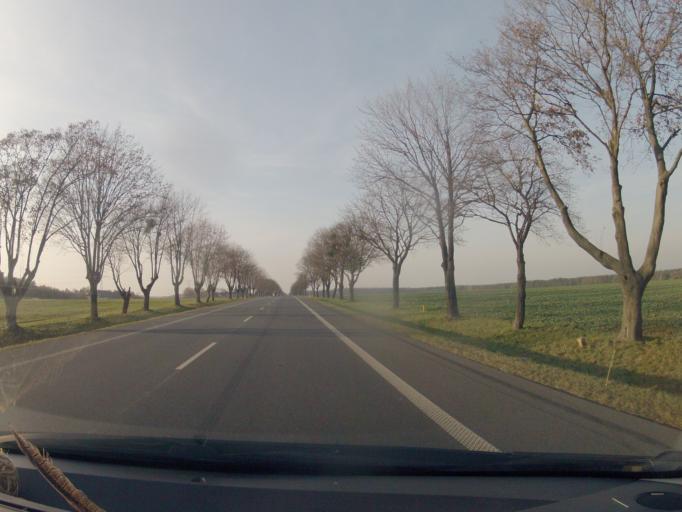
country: PL
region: Opole Voivodeship
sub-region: Powiat strzelecki
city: Strzelce Opolskie
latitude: 50.5291
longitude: 18.2665
